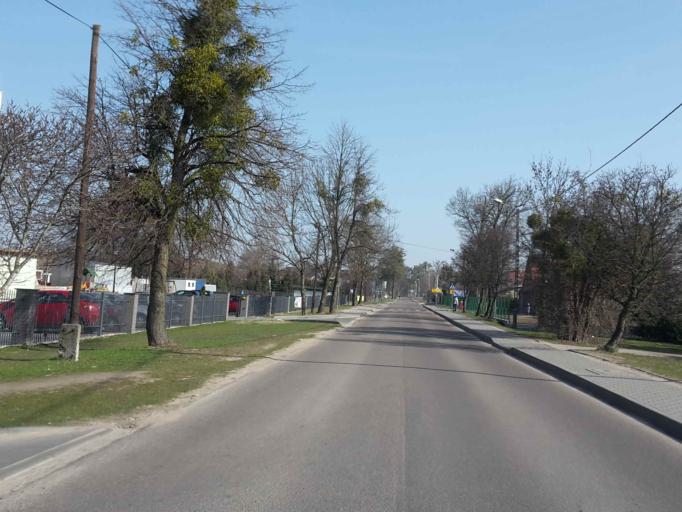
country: PL
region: Kujawsko-Pomorskie
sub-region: Powiat brodnicki
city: Brodnica
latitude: 53.2736
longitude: 19.4088
